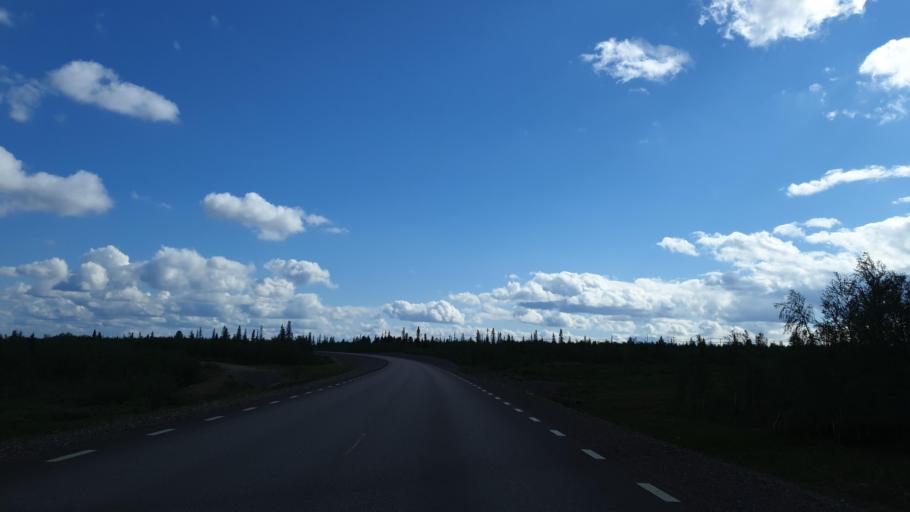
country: SE
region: Norrbotten
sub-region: Kiruna Kommun
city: Kiruna
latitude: 67.8081
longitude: 20.2339
